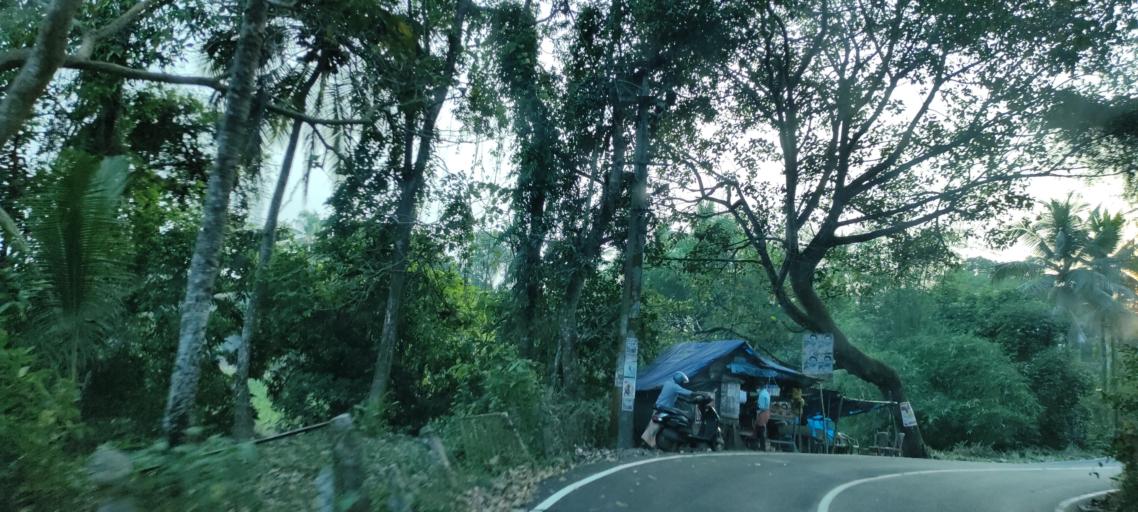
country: IN
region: Kerala
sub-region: Alappuzha
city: Mavelikara
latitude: 9.2701
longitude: 76.5515
